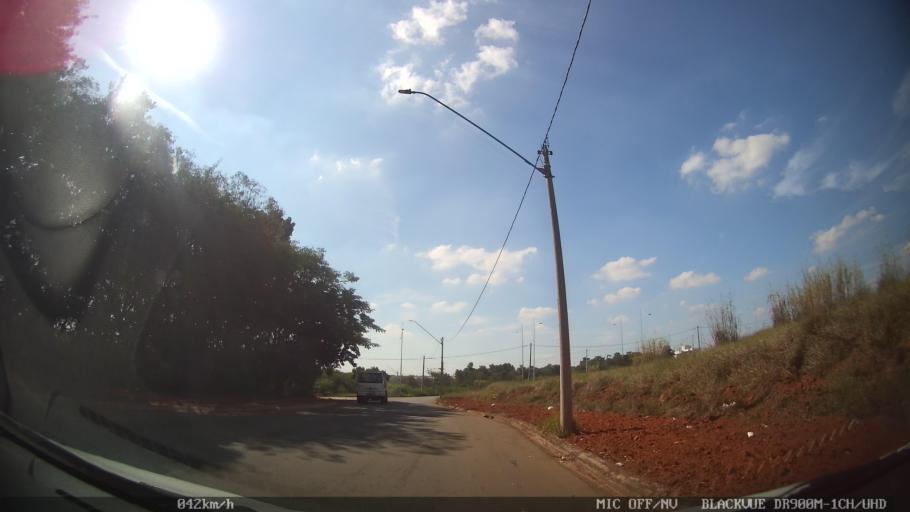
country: BR
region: Sao Paulo
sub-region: Hortolandia
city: Hortolandia
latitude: -22.8637
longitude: -47.2359
